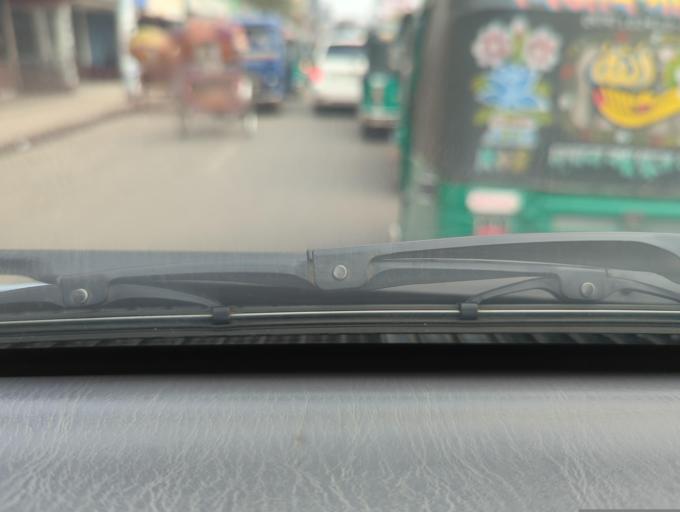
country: BD
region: Sylhet
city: Maulavi Bazar
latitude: 24.4898
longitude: 91.7587
